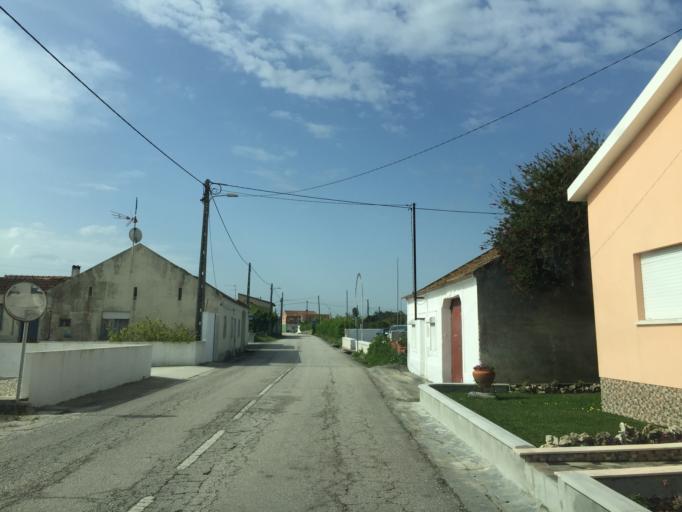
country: PT
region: Coimbra
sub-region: Figueira da Foz
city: Lavos
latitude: 40.0161
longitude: -8.8232
